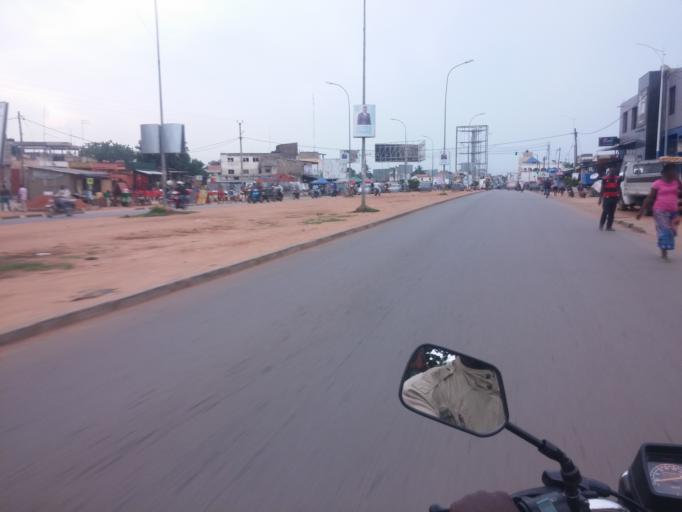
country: TG
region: Maritime
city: Lome
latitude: 6.1994
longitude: 1.1801
